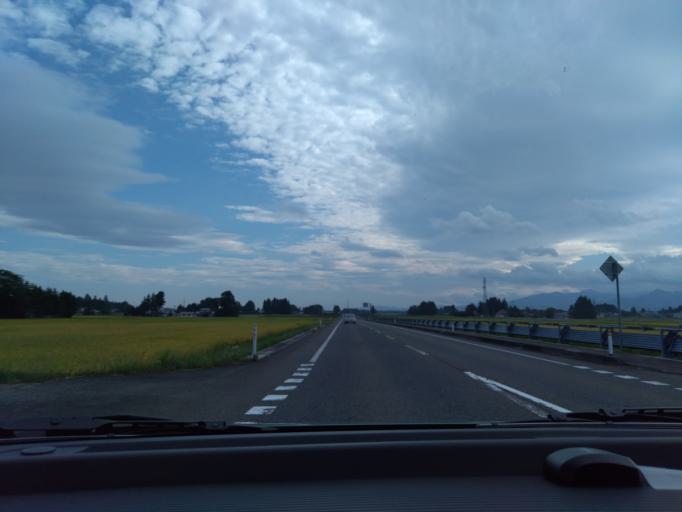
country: JP
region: Iwate
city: Hanamaki
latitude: 39.3561
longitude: 141.0546
